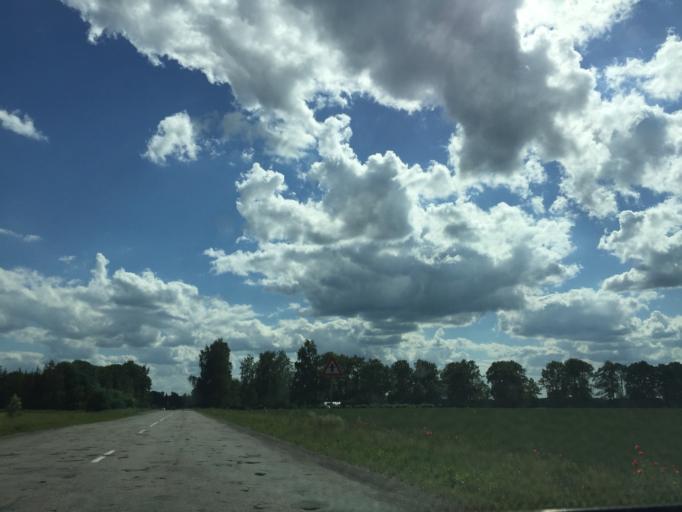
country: LV
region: Tukuma Rajons
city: Tukums
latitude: 56.8871
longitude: 23.0813
